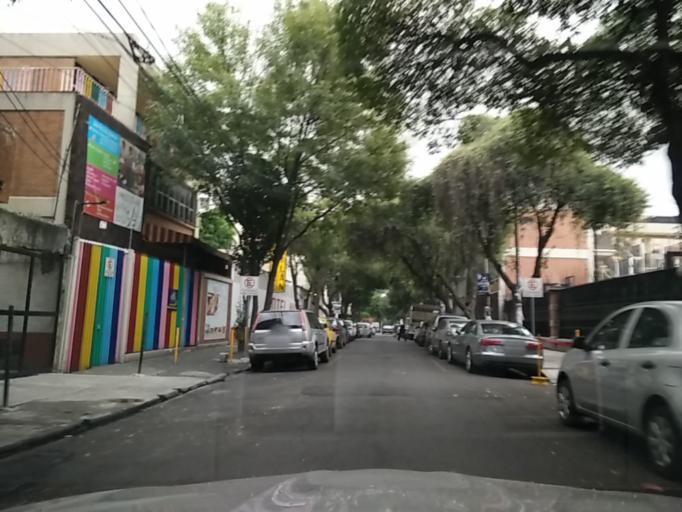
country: MX
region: Mexico City
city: Benito Juarez
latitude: 19.4176
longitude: -99.1594
